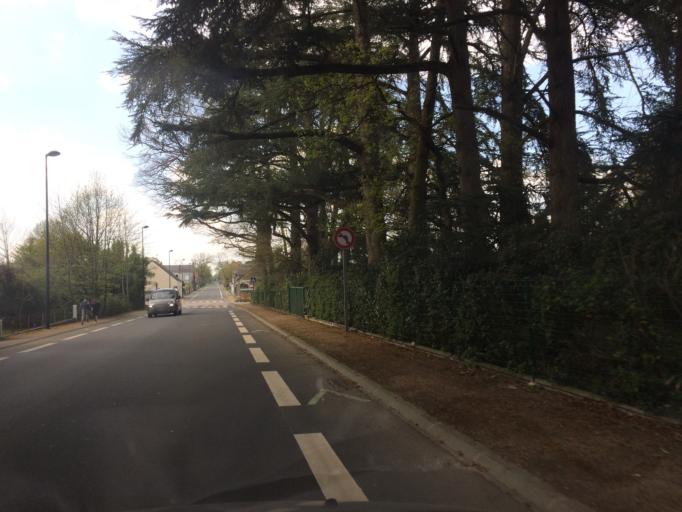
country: FR
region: Pays de la Loire
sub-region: Departement de la Loire-Atlantique
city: Heric
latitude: 47.4168
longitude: -1.6538
